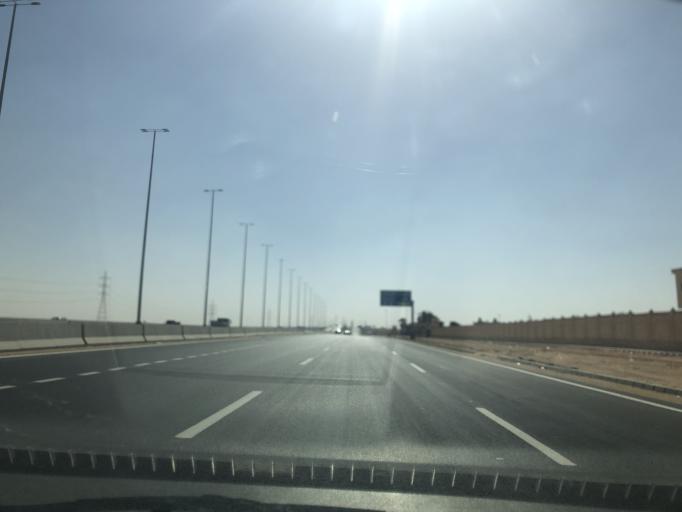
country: EG
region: Al Jizah
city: Madinat Sittah Uktubar
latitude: 29.8851
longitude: 31.0779
